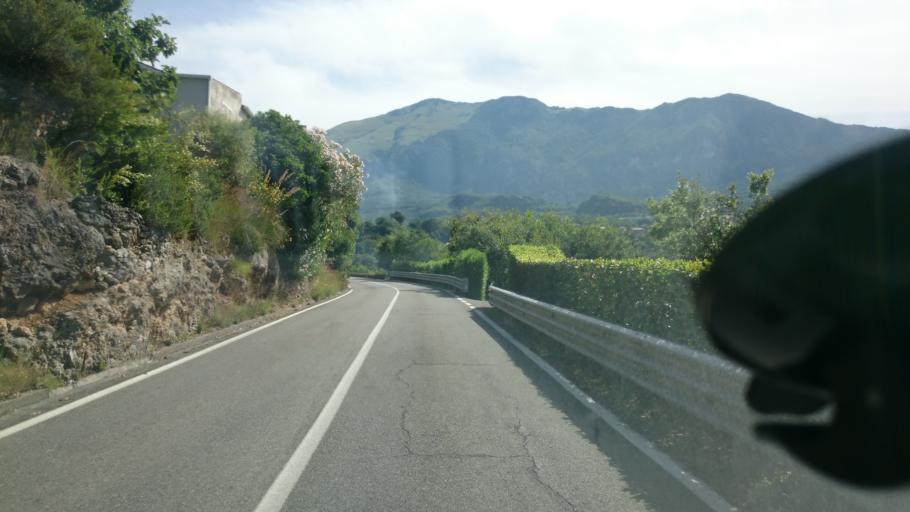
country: IT
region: Basilicate
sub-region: Provincia di Potenza
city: Maratea
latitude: 39.9939
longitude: 15.7072
